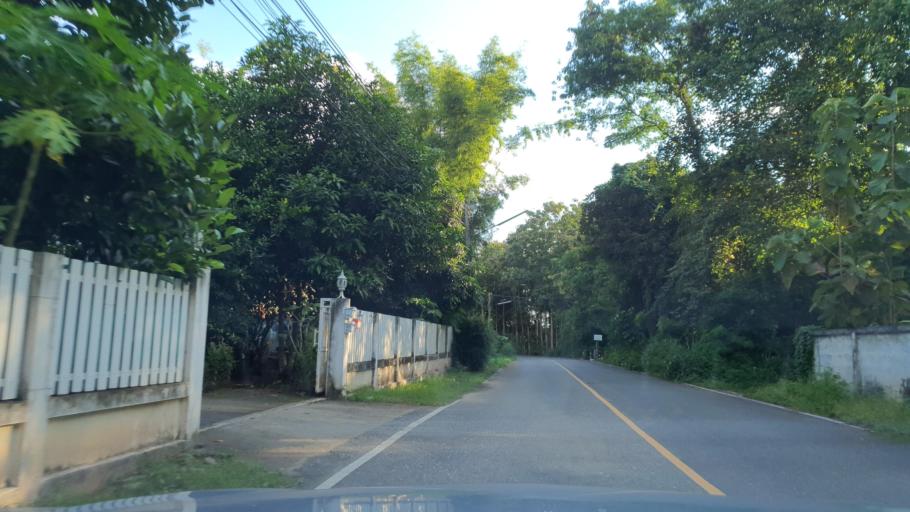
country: TH
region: Chiang Mai
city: San Sai
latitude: 18.8674
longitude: 99.1508
